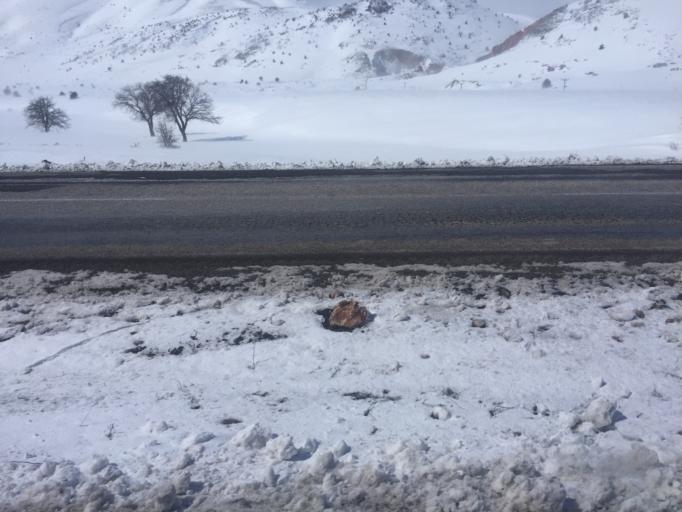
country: TR
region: Kahramanmaras
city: Goksun
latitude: 38.1828
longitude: 36.4566
